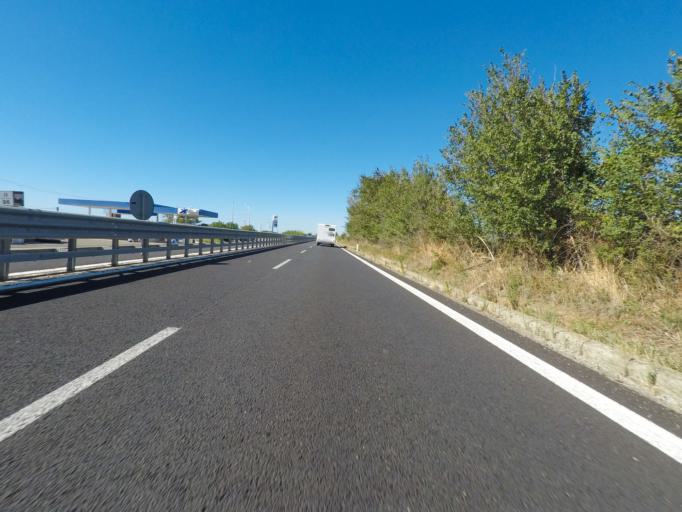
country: IT
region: Latium
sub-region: Provincia di Viterbo
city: Tarquinia
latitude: 42.2731
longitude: 11.7101
